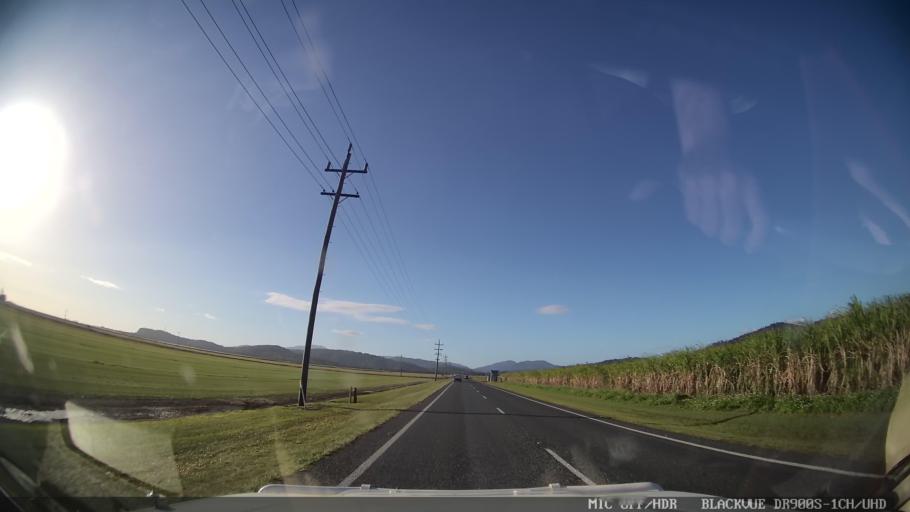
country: AU
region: Queensland
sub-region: Whitsunday
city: Proserpine
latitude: -20.3871
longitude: 148.5868
